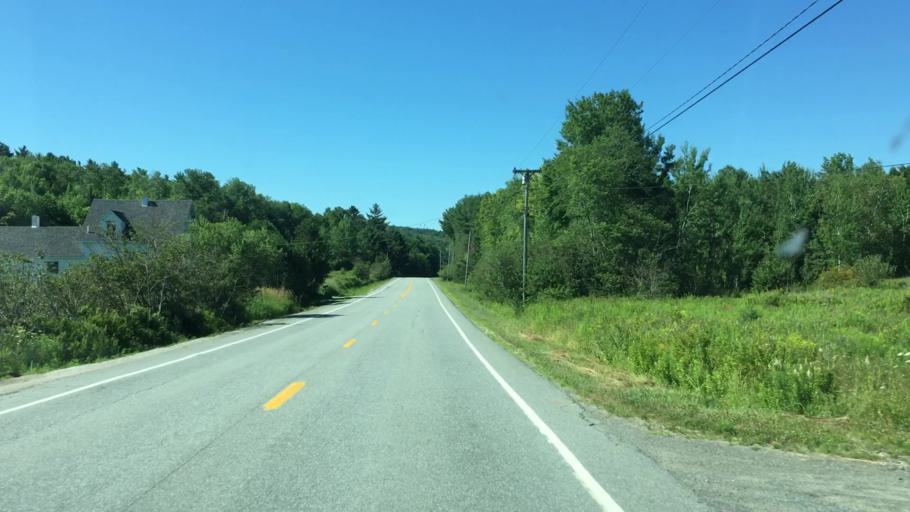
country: US
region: Maine
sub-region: Hancock County
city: Dedham
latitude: 44.6706
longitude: -68.6729
